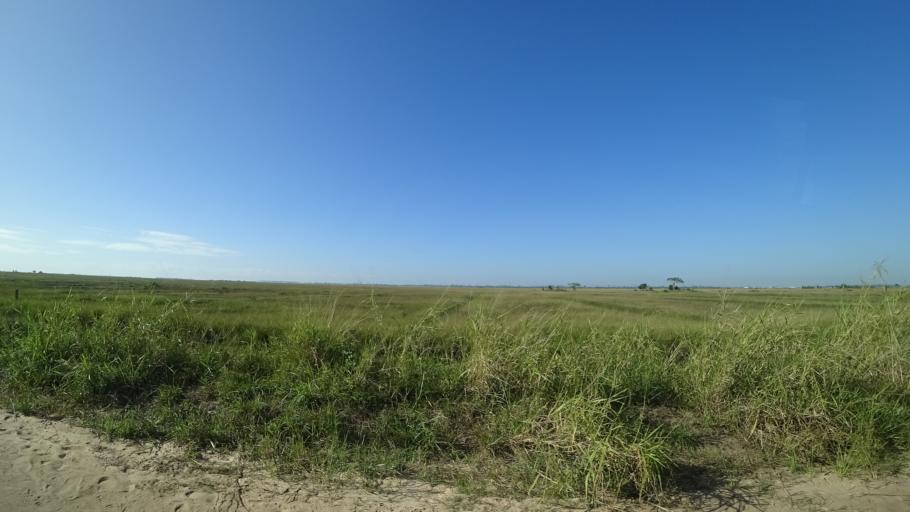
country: MZ
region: Sofala
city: Beira
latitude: -19.7593
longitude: 34.9157
